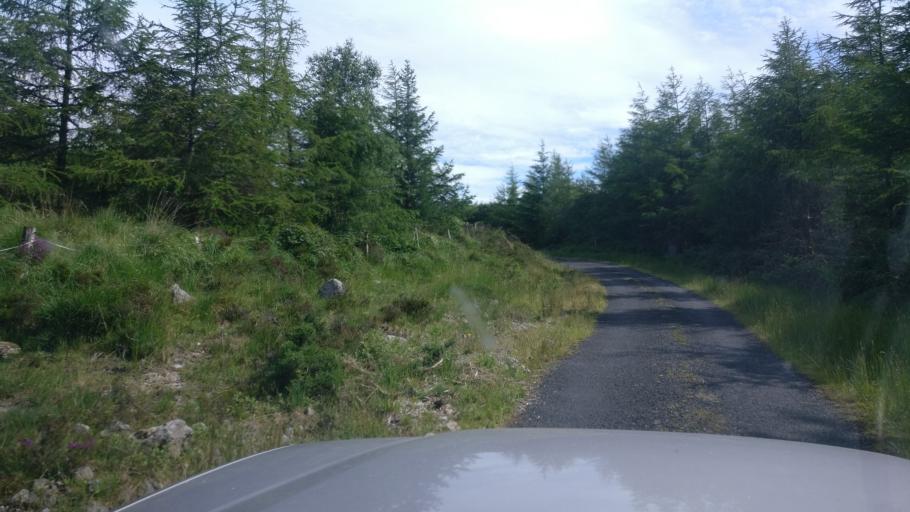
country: IE
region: Connaught
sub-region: County Galway
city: Gort
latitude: 53.0850
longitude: -8.6928
